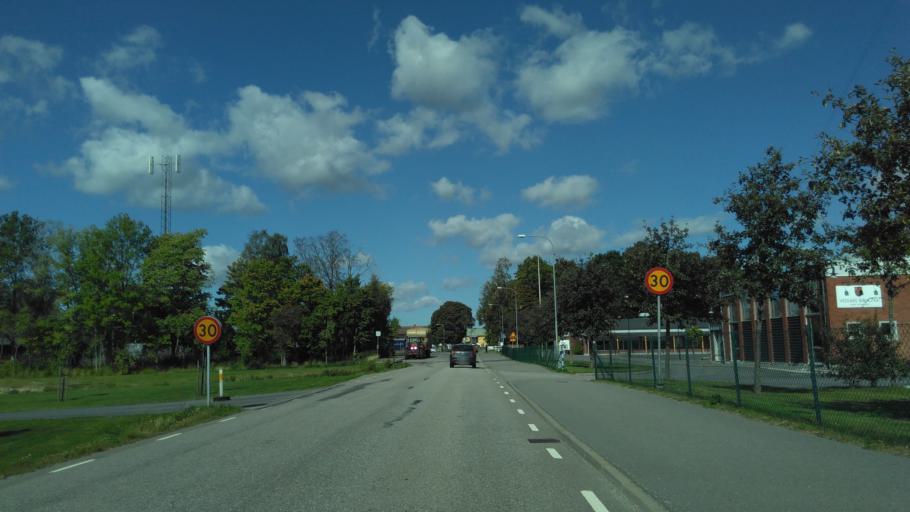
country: SE
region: Vaestra Goetaland
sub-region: Herrljunga Kommun
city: Herrljunga
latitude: 58.1681
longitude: 13.0008
